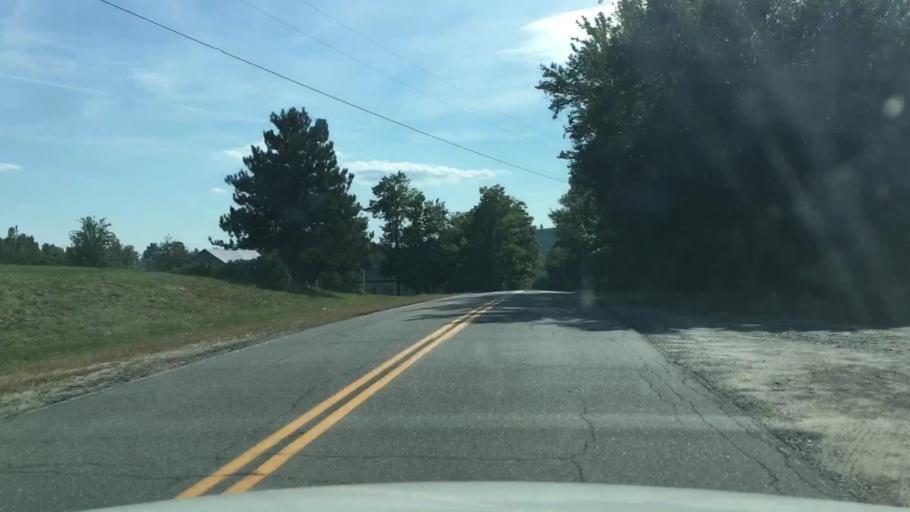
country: US
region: Maine
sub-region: Penobscot County
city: Enfield
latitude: 45.3021
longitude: -68.5490
